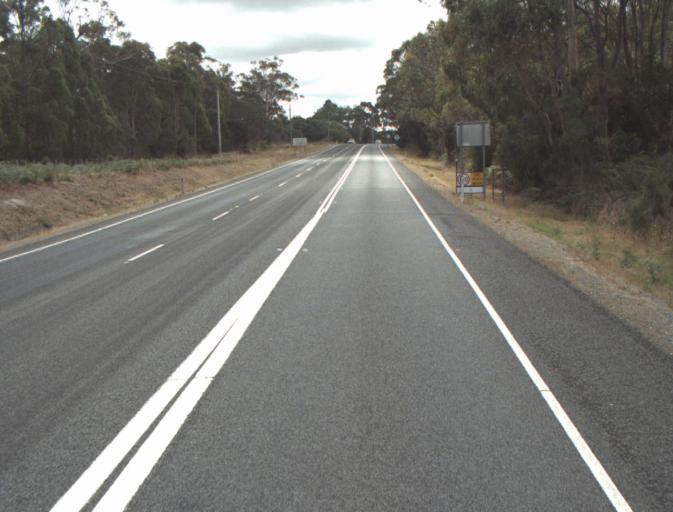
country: AU
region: Tasmania
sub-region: Launceston
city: Mayfield
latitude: -41.2884
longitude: 147.0422
